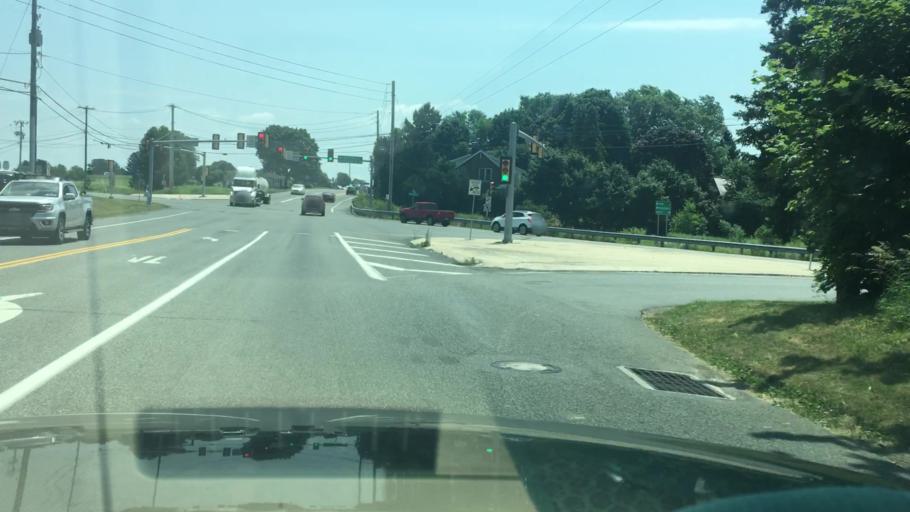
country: US
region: Pennsylvania
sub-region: Lehigh County
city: Schnecksville
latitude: 40.6146
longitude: -75.6547
